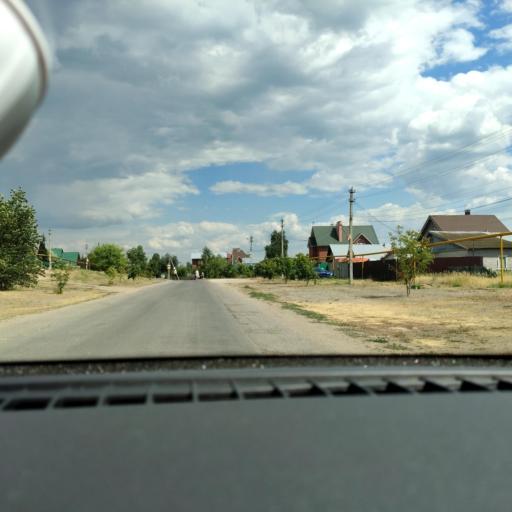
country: RU
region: Samara
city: Volzhskiy
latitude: 53.4277
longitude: 50.1261
